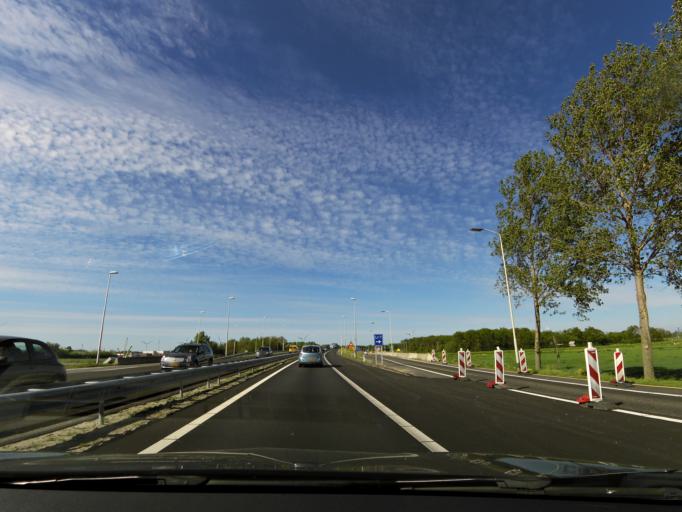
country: NL
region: South Holland
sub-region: Gemeente Brielle
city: Brielle
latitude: 51.8872
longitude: 4.1949
